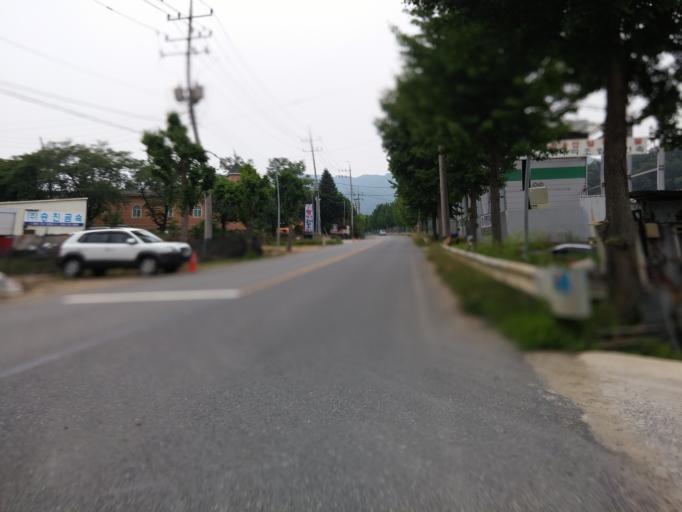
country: KR
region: Chungcheongbuk-do
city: Okcheon
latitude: 36.2997
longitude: 127.5396
